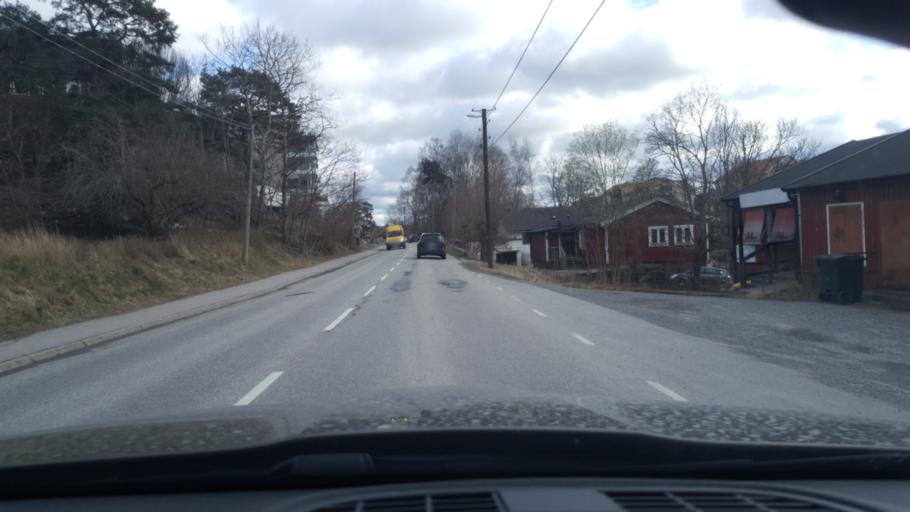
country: SE
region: Stockholm
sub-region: Osterakers Kommun
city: Akersberga
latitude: 59.4838
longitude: 18.2918
